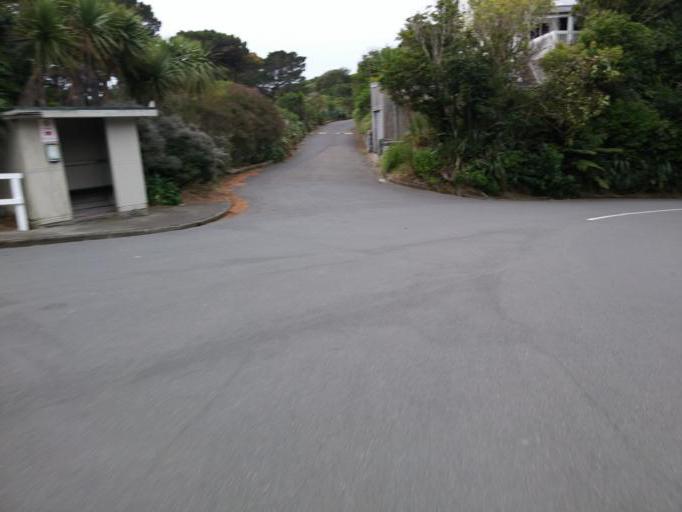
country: NZ
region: Wellington
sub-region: Wellington City
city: Kelburn
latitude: -41.2942
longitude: 174.7532
